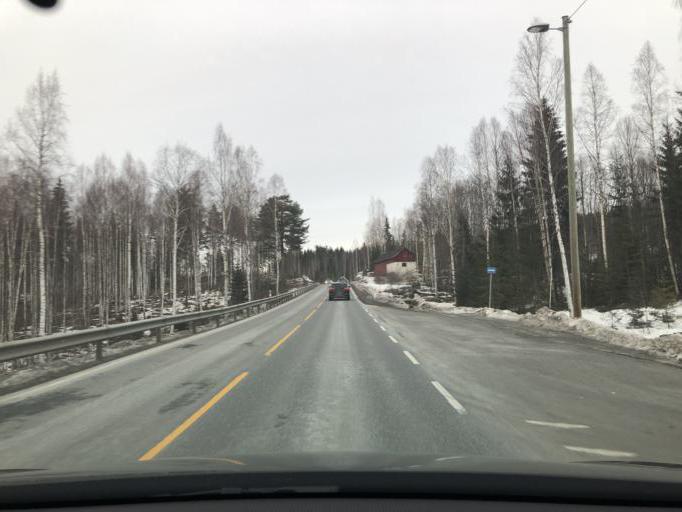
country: NO
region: Oppland
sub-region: Nordre Land
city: Dokka
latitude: 60.4976
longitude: 10.0742
